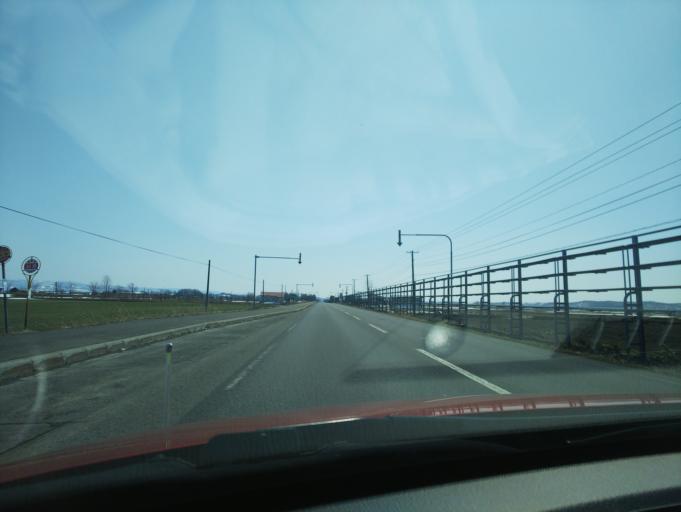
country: JP
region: Hokkaido
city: Nayoro
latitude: 44.2305
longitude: 142.3948
